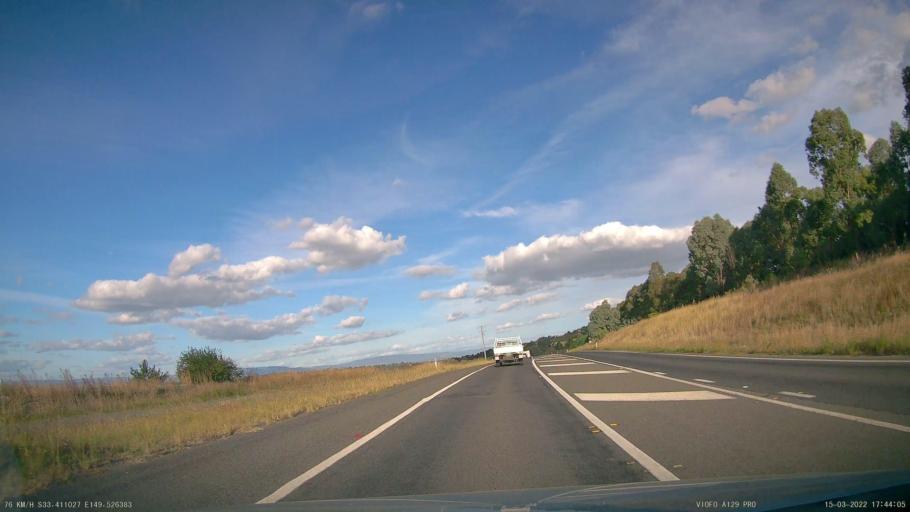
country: AU
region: New South Wales
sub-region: Bathurst Regional
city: Eglinton
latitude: -33.4110
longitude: 149.5265
